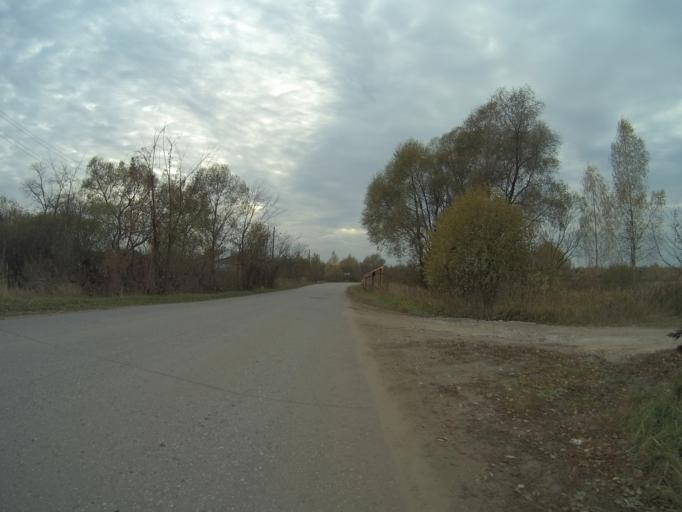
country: RU
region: Vladimir
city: Orgtrud
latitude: 56.1558
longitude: 40.5972
